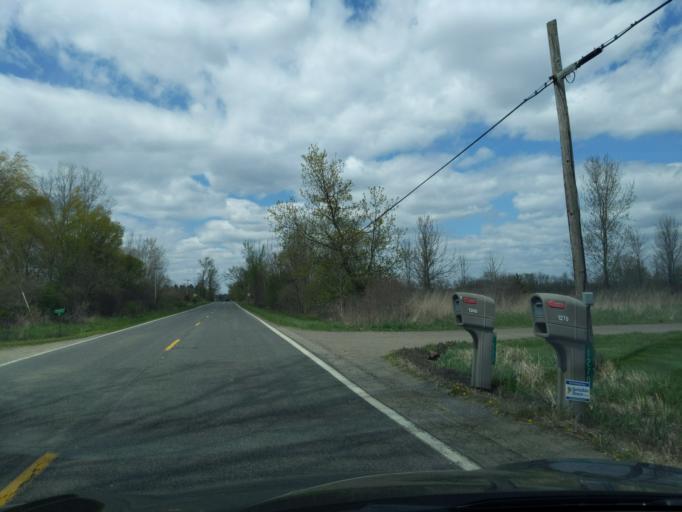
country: US
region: Michigan
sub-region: Ingham County
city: Mason
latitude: 42.6184
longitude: -84.4574
